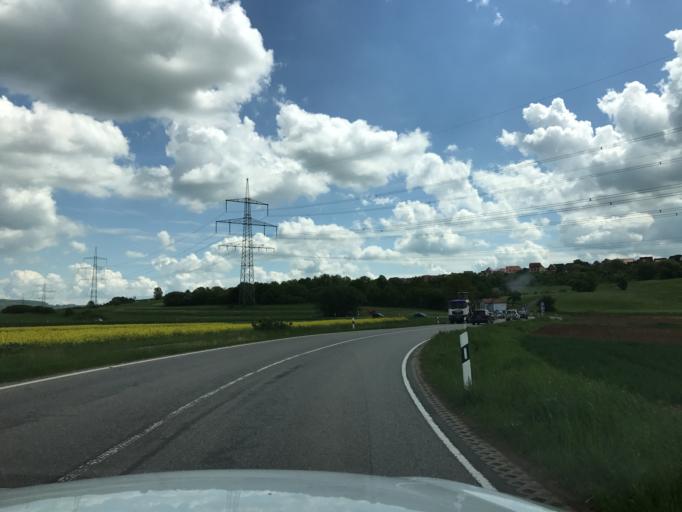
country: DE
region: Bavaria
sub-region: Upper Franconia
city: Pinzberg
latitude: 49.6985
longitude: 11.0983
